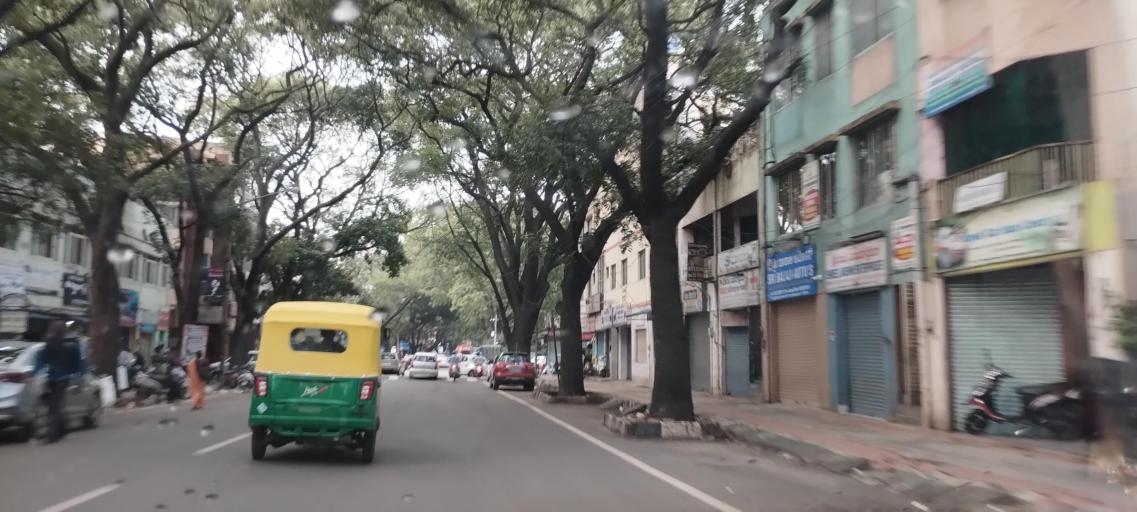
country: IN
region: Karnataka
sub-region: Bangalore Urban
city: Bangalore
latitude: 12.9537
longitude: 77.5782
